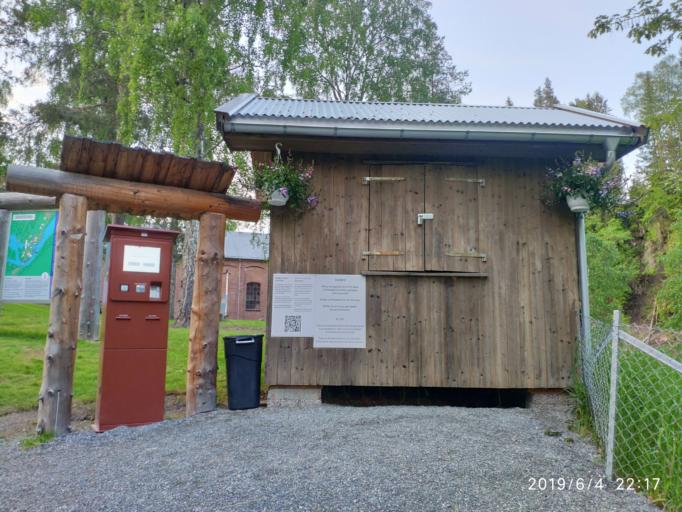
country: NO
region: Oppland
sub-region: Jevnaker
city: Jevnaker
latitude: 60.2212
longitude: 10.3690
